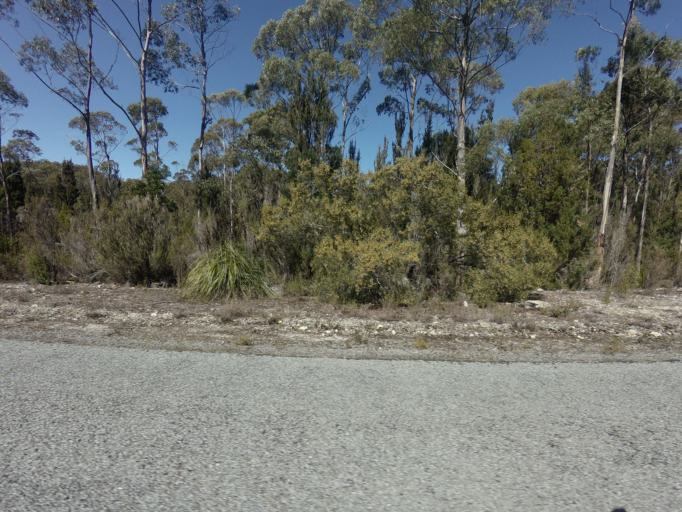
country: AU
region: Tasmania
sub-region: Huon Valley
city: Geeveston
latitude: -42.7697
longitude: 146.3968
